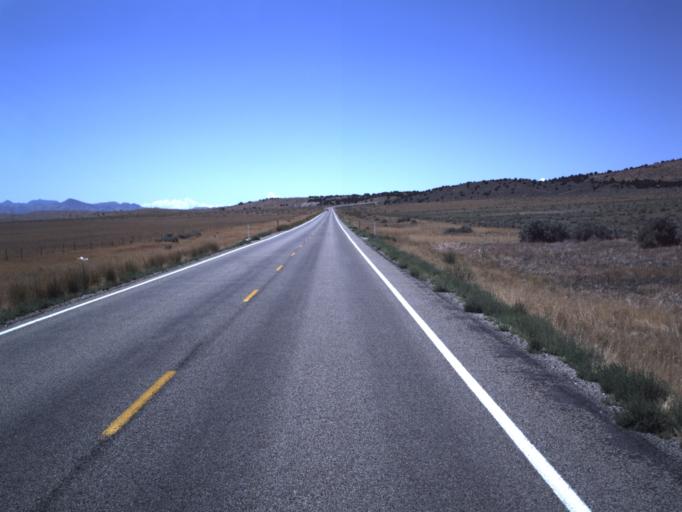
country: US
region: Utah
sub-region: Juab County
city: Nephi
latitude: 39.6756
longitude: -112.0227
